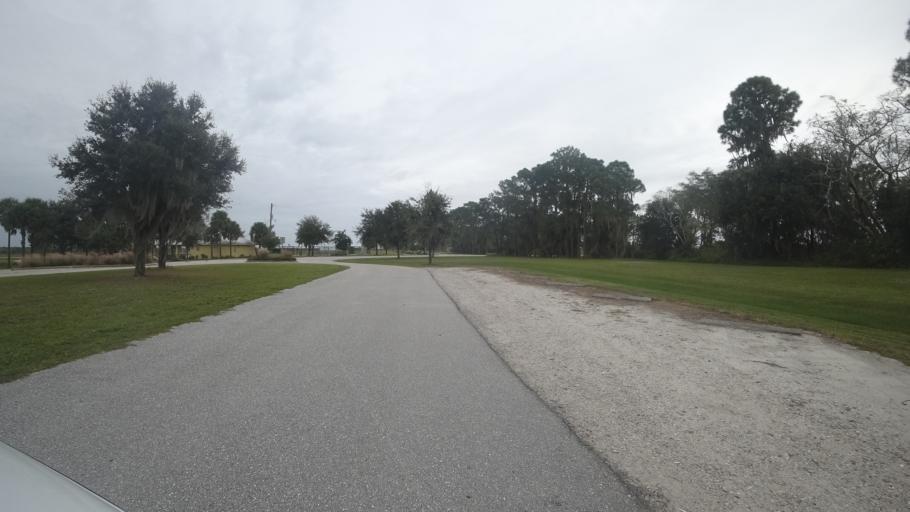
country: US
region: Florida
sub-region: Hillsborough County
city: Wimauma
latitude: 27.5844
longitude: -82.1773
